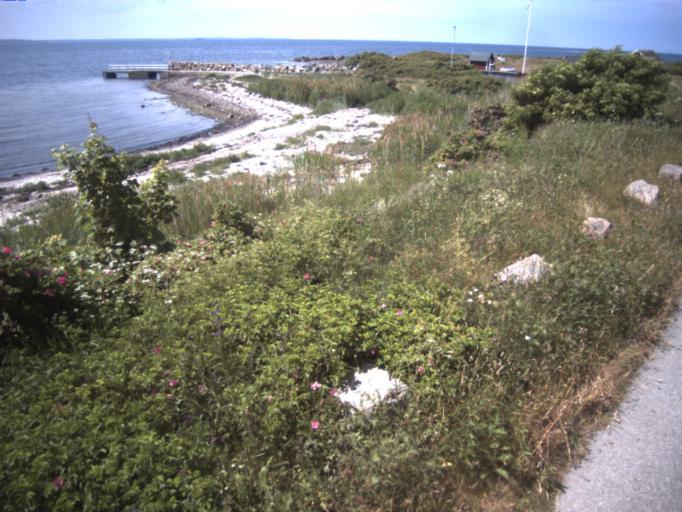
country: DK
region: Capital Region
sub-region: Helsingor Kommune
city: Hellebaek
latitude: 56.1212
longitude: 12.6018
